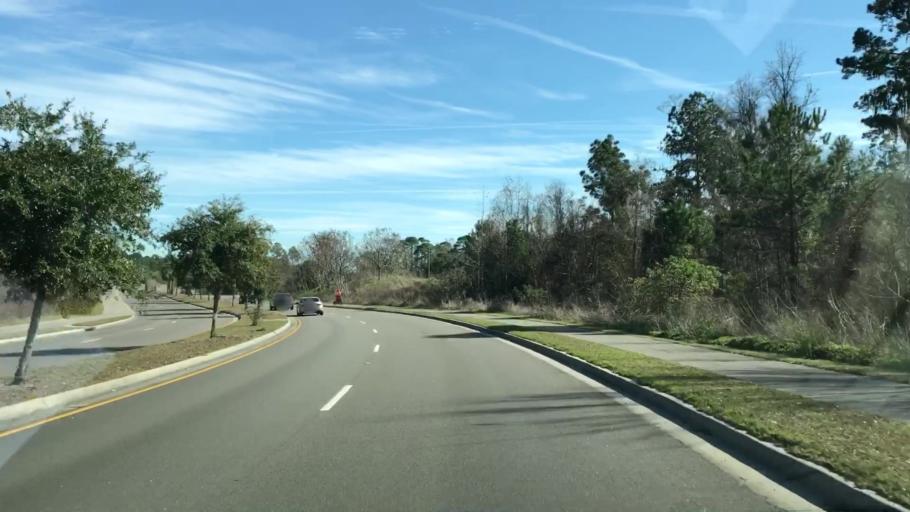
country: US
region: South Carolina
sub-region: Beaufort County
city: Bluffton
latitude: 32.2625
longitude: -80.8761
